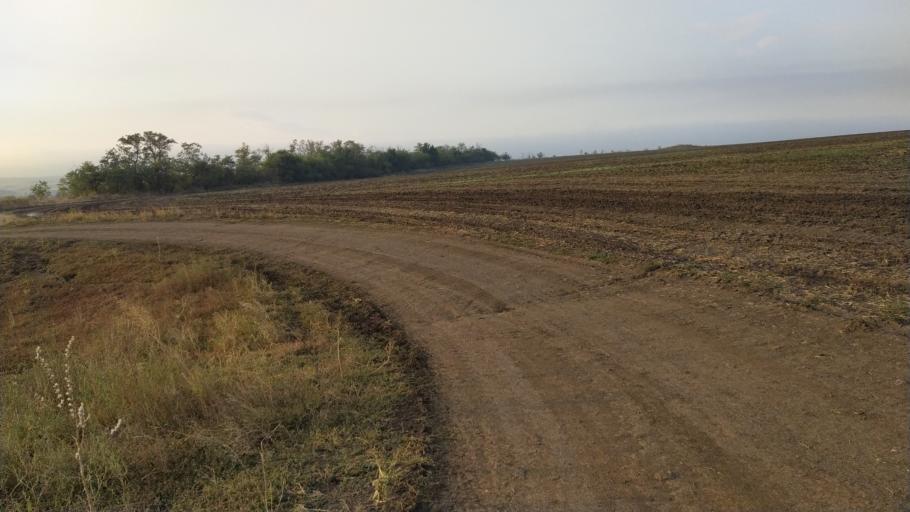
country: RU
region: Rostov
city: Gornyy
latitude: 47.8910
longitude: 40.2402
